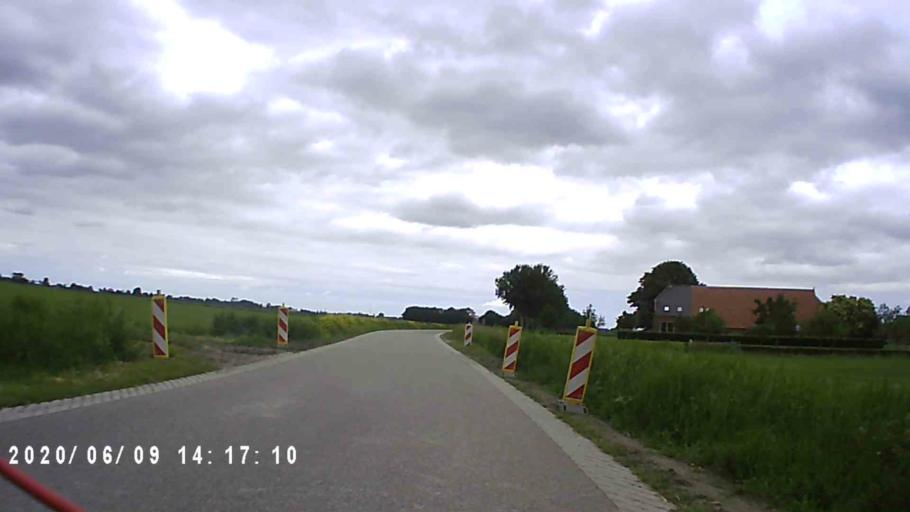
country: NL
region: Groningen
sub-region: Gemeente Bedum
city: Bedum
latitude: 53.2827
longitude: 6.5930
